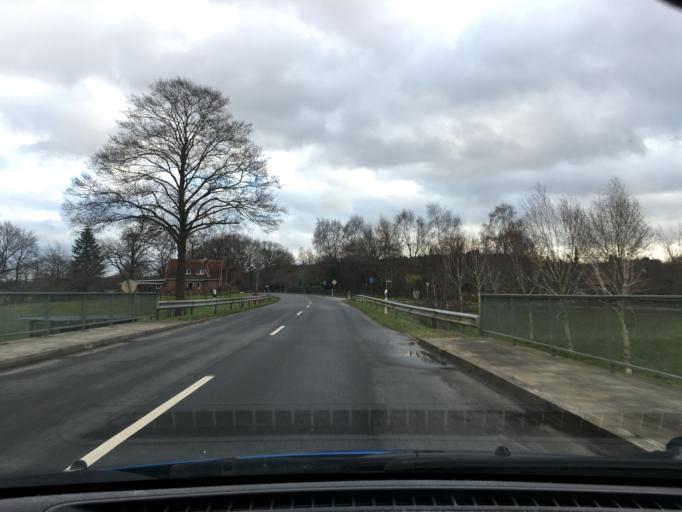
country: DE
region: Schleswig-Holstein
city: Kaaks
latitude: 53.9879
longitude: 9.4787
